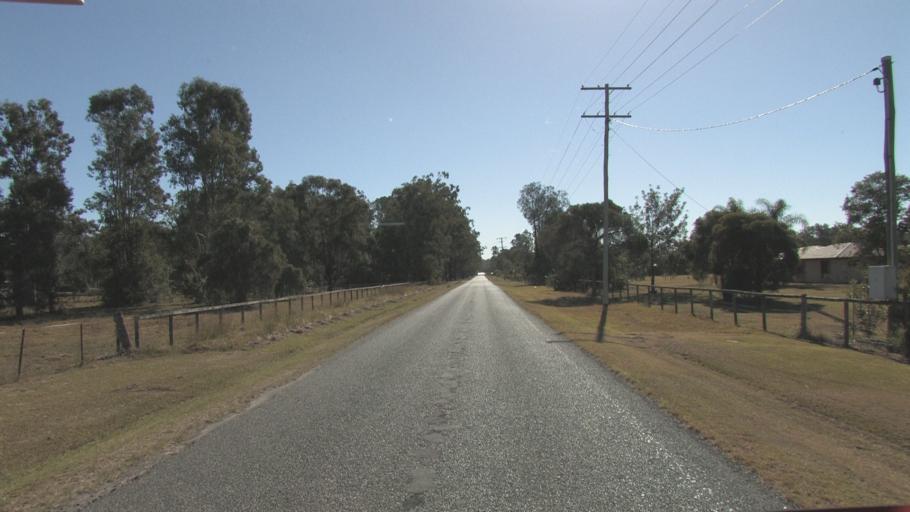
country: AU
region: Queensland
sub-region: Logan
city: Chambers Flat
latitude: -27.7560
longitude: 153.0758
